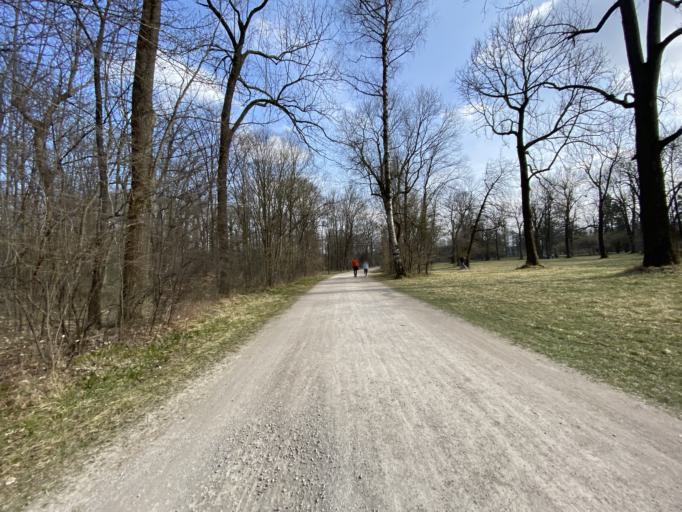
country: DE
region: Bavaria
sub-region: Upper Bavaria
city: Bogenhausen
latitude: 48.1714
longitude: 11.6147
